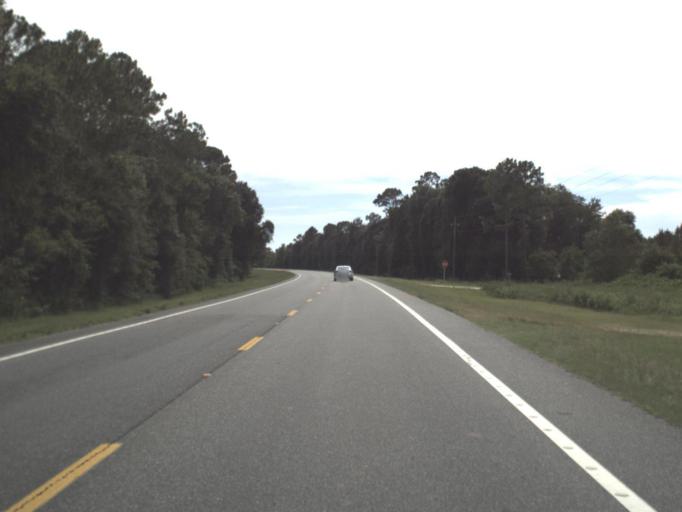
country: US
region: Florida
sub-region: Taylor County
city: Perry
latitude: 30.0950
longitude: -83.4864
